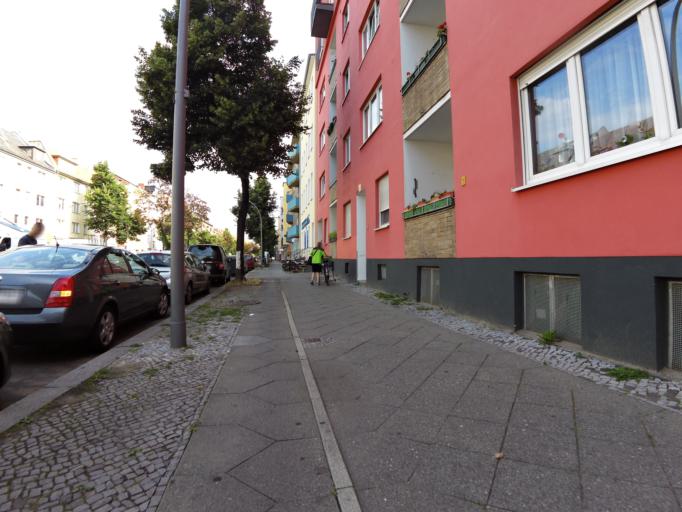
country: DE
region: Berlin
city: Lichterfelde
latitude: 52.4437
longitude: 13.3158
